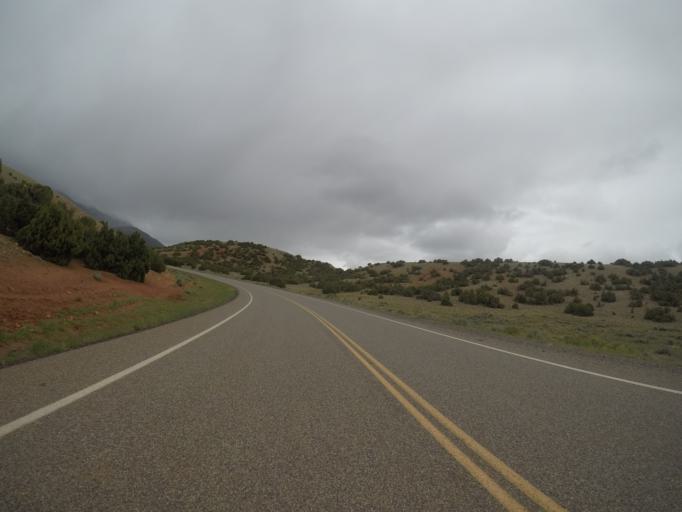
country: US
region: Wyoming
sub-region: Big Horn County
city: Lovell
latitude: 45.1035
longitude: -108.2374
